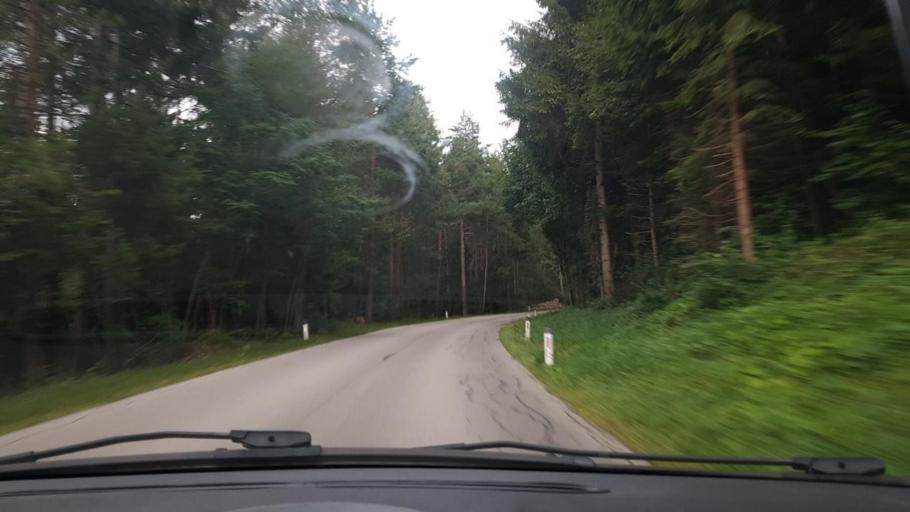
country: AT
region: Tyrol
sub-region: Politischer Bezirk Lienz
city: Amlach
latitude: 46.8127
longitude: 12.7754
